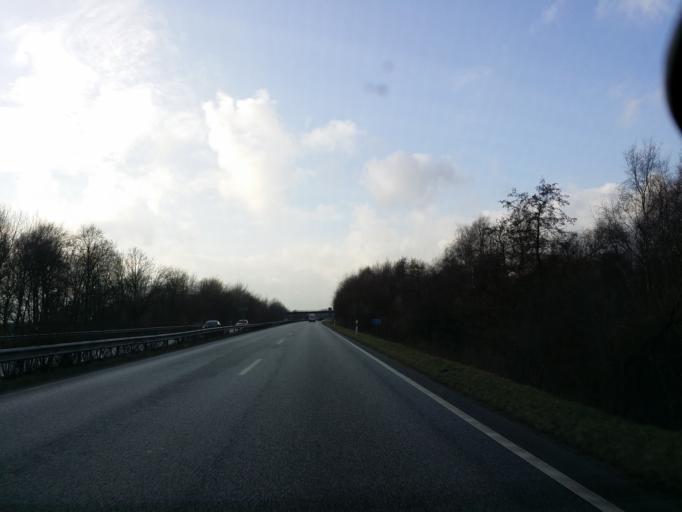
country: DE
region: Schleswig-Holstein
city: Bredenbek
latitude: 54.3149
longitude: 9.8756
